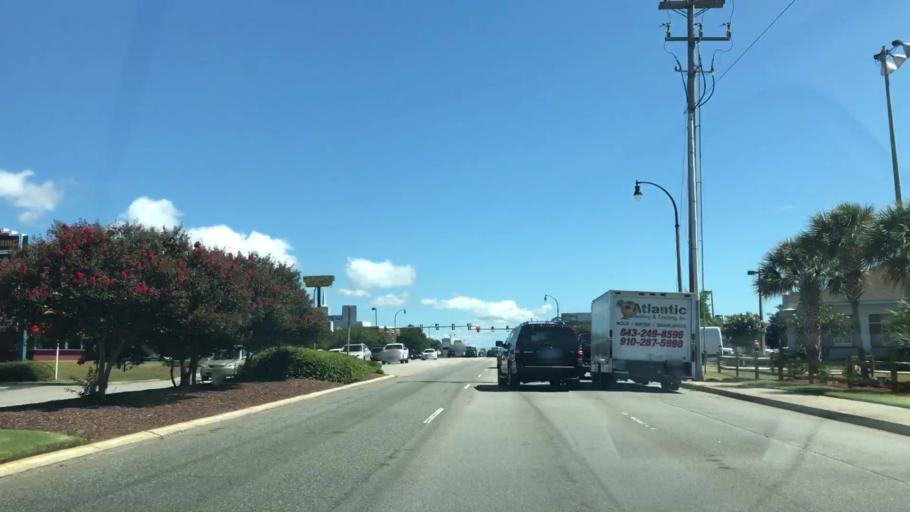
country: US
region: South Carolina
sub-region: Horry County
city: North Myrtle Beach
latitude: 33.8235
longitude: -78.6857
